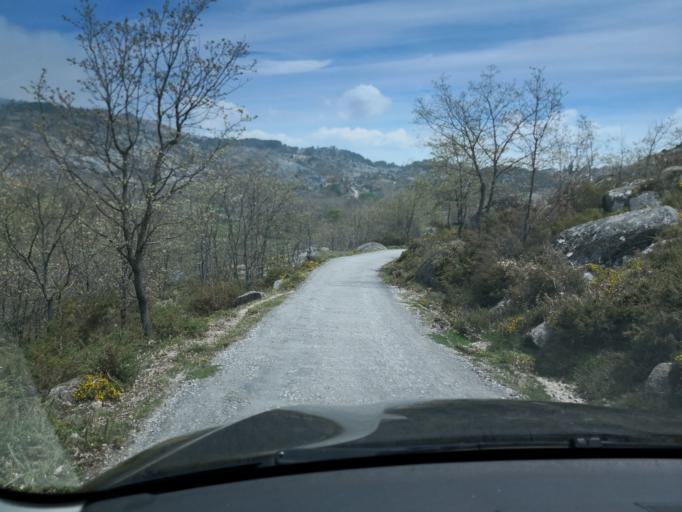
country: PT
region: Vila Real
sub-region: Vila Real
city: Vila Real
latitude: 41.3338
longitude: -7.8041
